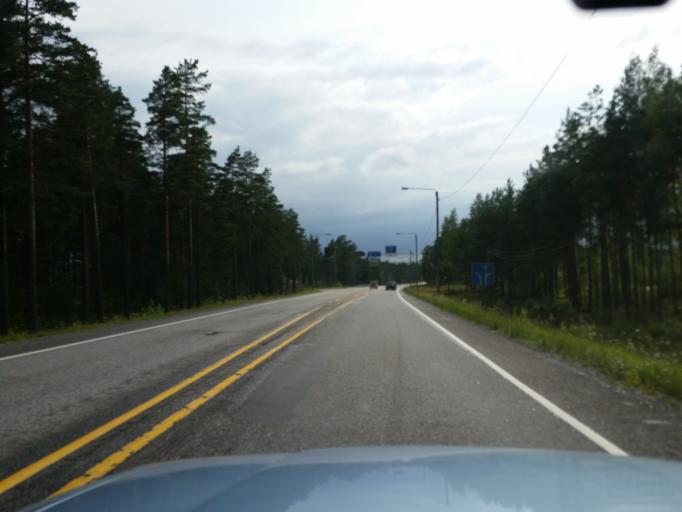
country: FI
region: Uusimaa
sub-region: Raaseporin
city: Pohja
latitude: 60.0191
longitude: 23.5697
